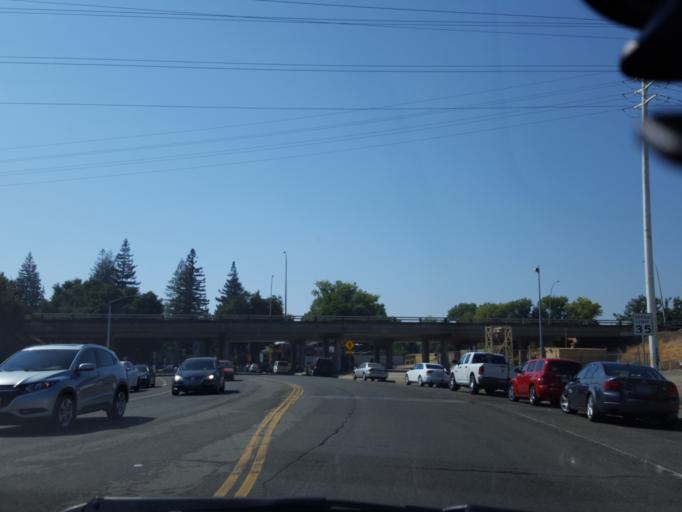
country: US
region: California
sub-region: Sacramento County
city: Rosemont
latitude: 38.5577
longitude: -121.4080
